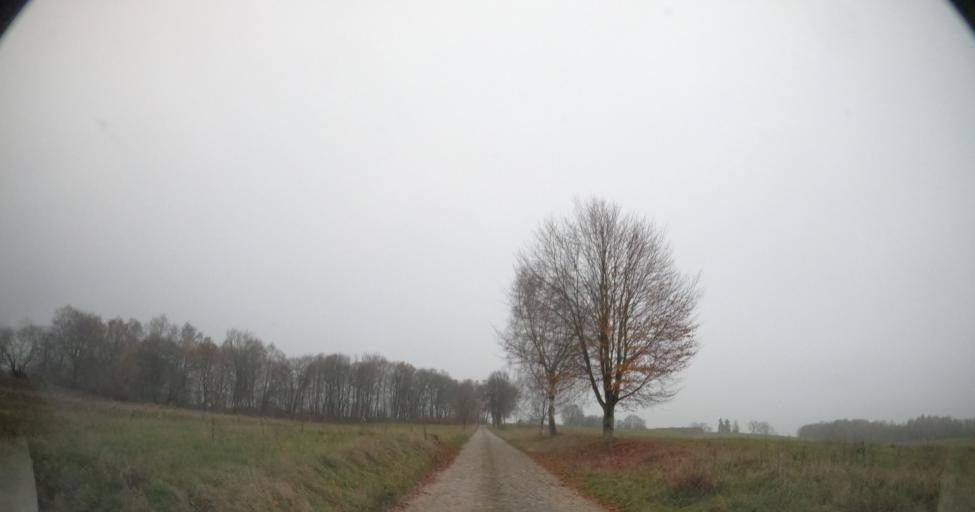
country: PL
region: West Pomeranian Voivodeship
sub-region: Powiat drawski
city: Drawsko Pomorskie
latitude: 53.5454
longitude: 15.7277
